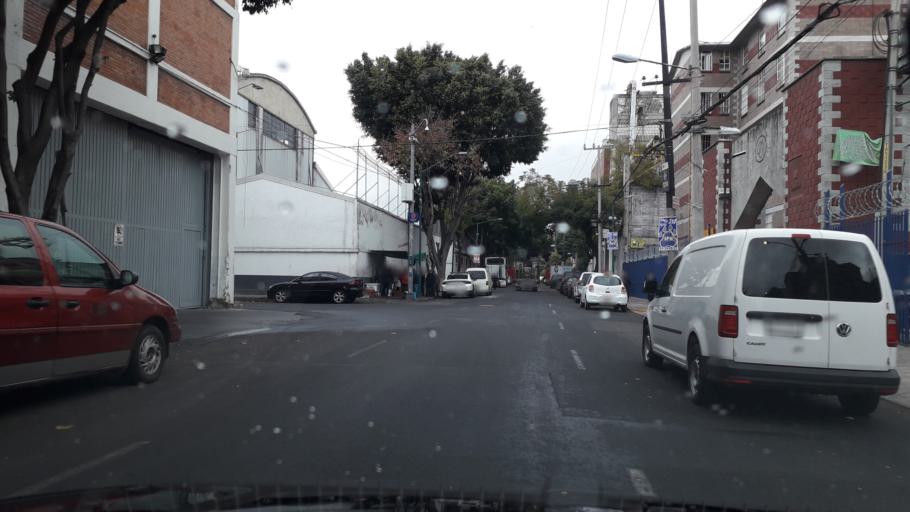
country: MX
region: Mexico City
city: Cuauhtemoc
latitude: 19.4568
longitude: -99.1573
